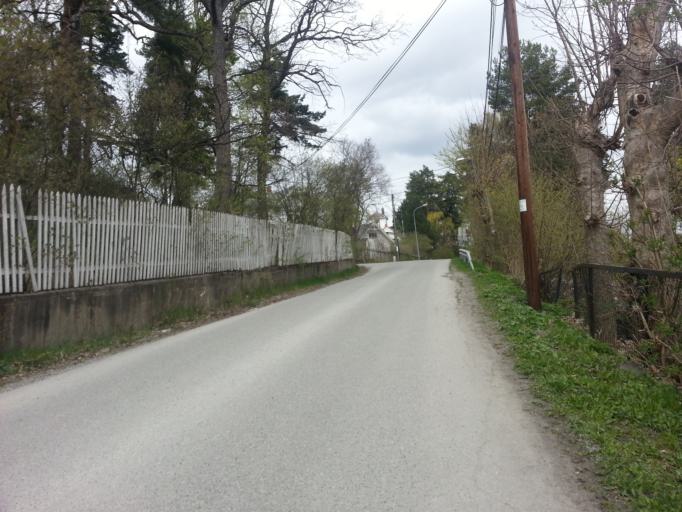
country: NO
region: Akershus
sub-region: Baerum
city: Lysaker
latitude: 59.9076
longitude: 10.6377
